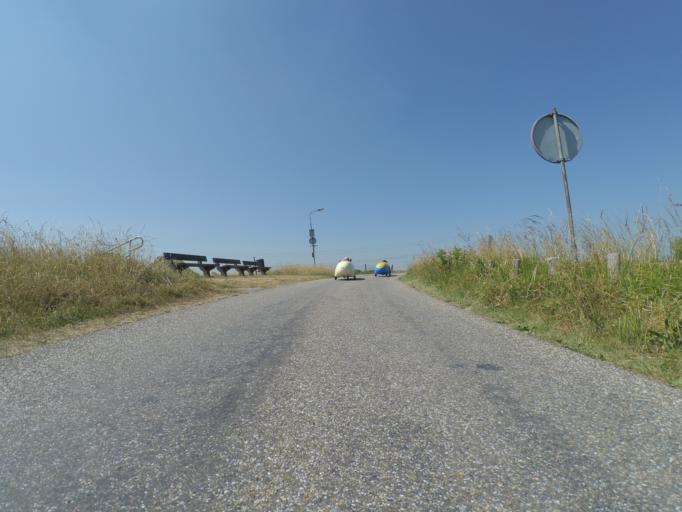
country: NL
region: Zeeland
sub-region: Gemeente Reimerswaal
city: Yerseke
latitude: 51.4351
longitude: 4.1264
